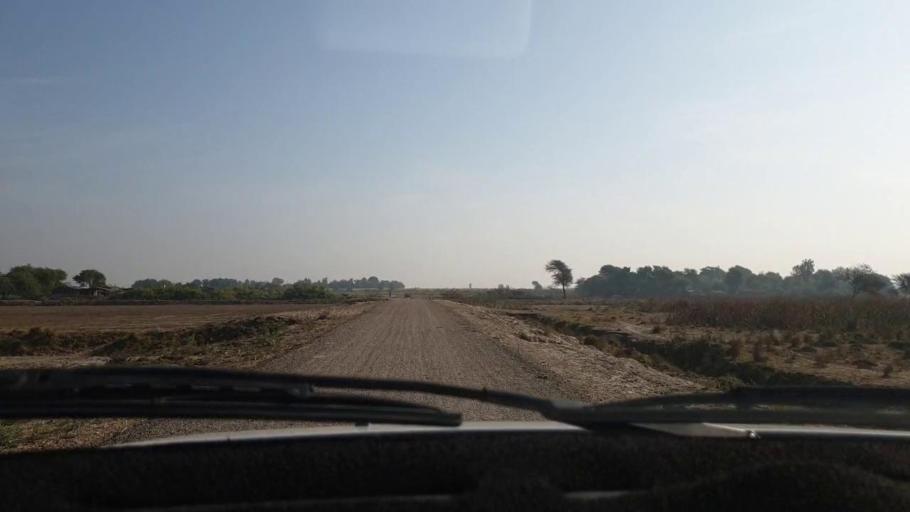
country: PK
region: Sindh
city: Tando Muhammad Khan
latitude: 25.0278
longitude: 68.4789
